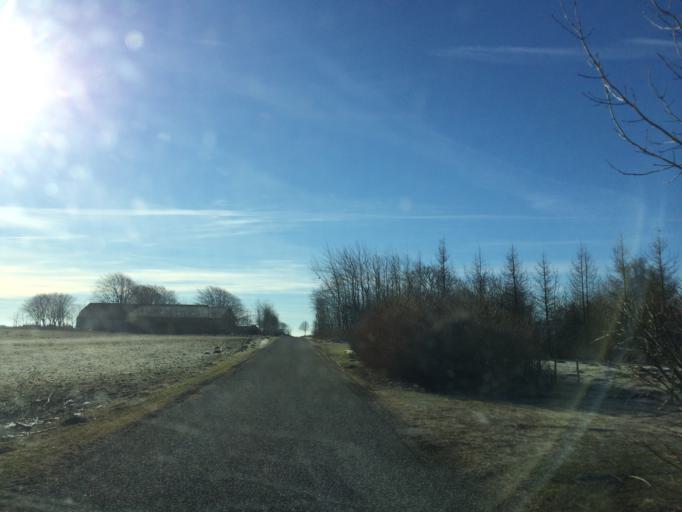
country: DK
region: North Denmark
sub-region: Mariagerfjord Kommune
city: Hobro
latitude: 56.6351
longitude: 9.6421
